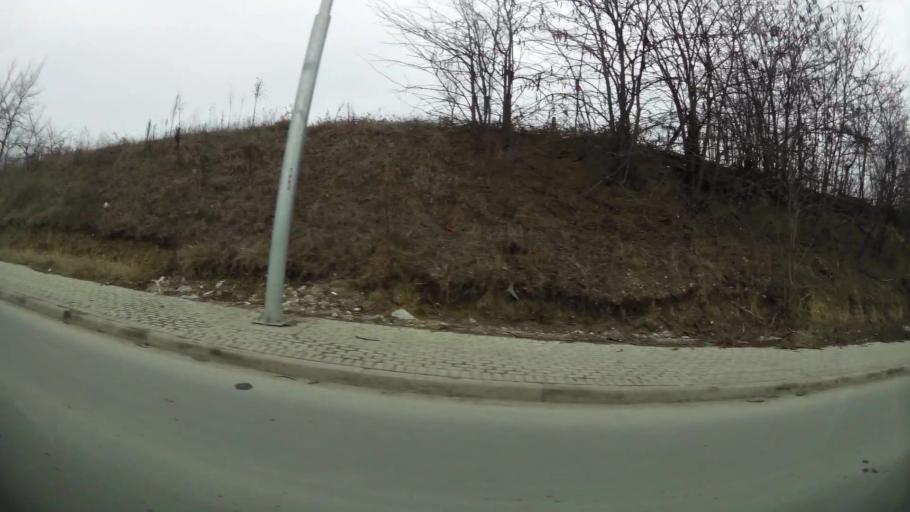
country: MK
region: Butel
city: Butel
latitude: 42.0384
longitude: 21.4410
